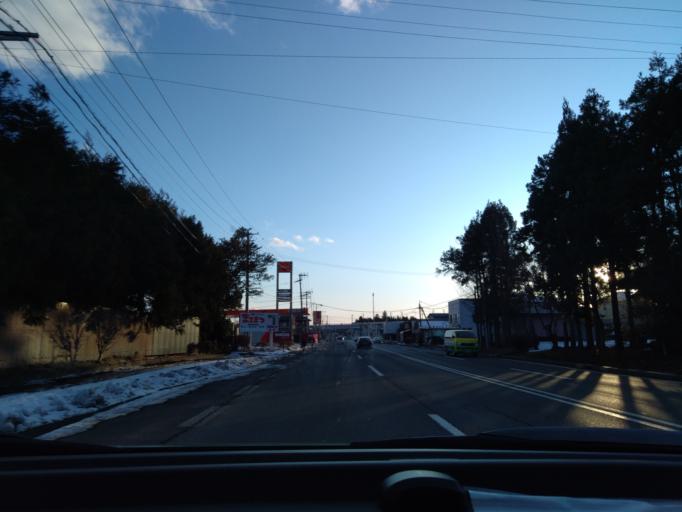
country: JP
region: Iwate
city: Hanamaki
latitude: 39.5395
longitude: 141.1690
